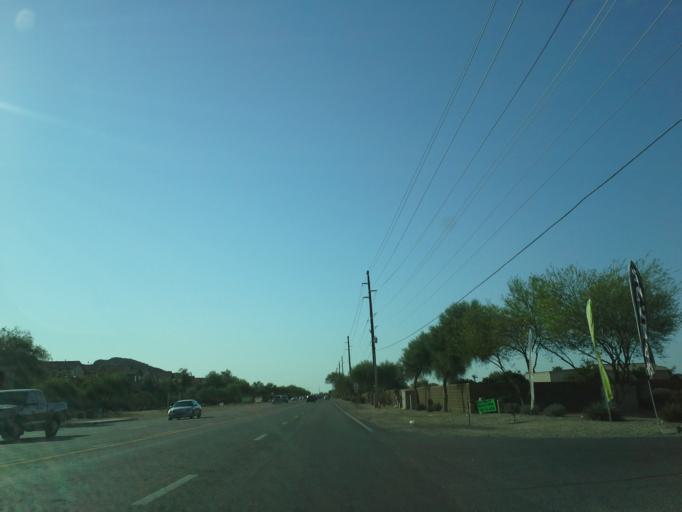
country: US
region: Arizona
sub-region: Pinal County
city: San Tan Valley
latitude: 33.1624
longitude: -111.5640
